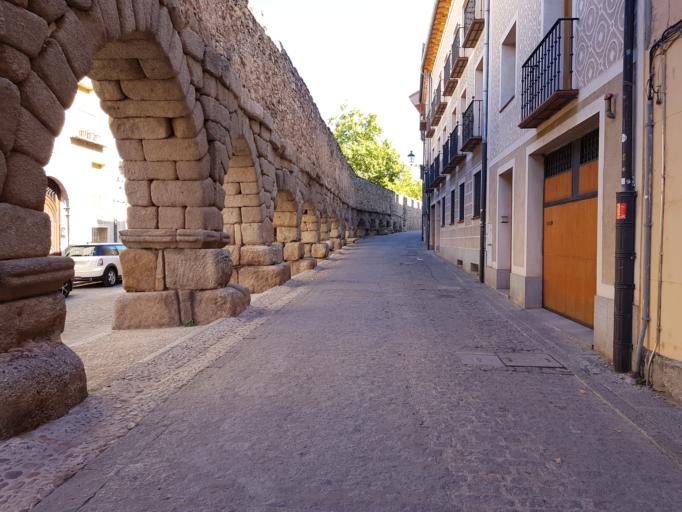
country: ES
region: Castille and Leon
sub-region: Provincia de Segovia
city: Segovia
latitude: 40.9459
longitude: -4.1125
